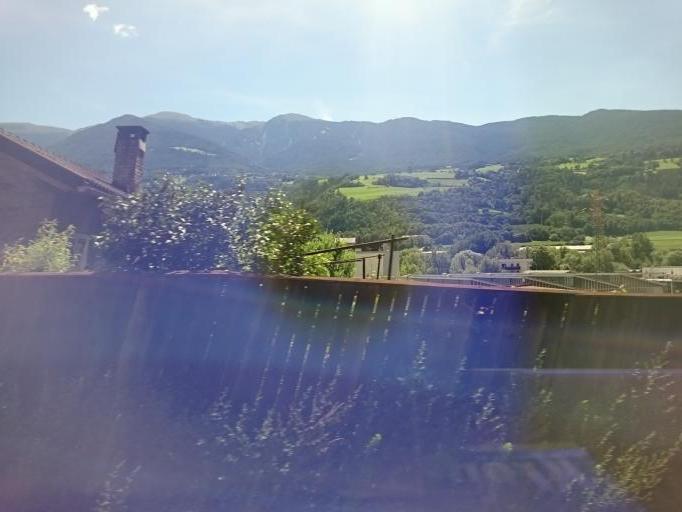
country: IT
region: Trentino-Alto Adige
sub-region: Bolzano
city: Bressanone
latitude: 46.7025
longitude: 11.6478
